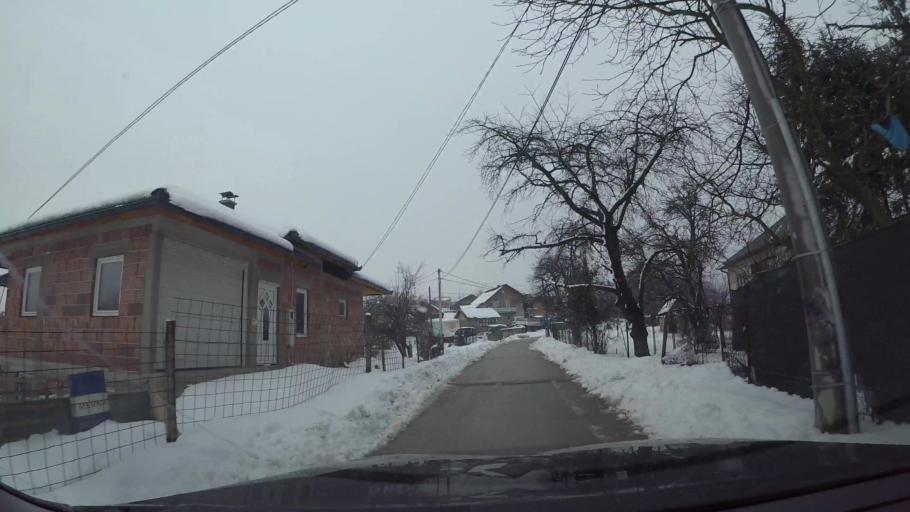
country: BA
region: Federation of Bosnia and Herzegovina
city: Hadzici
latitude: 43.8529
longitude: 18.2658
